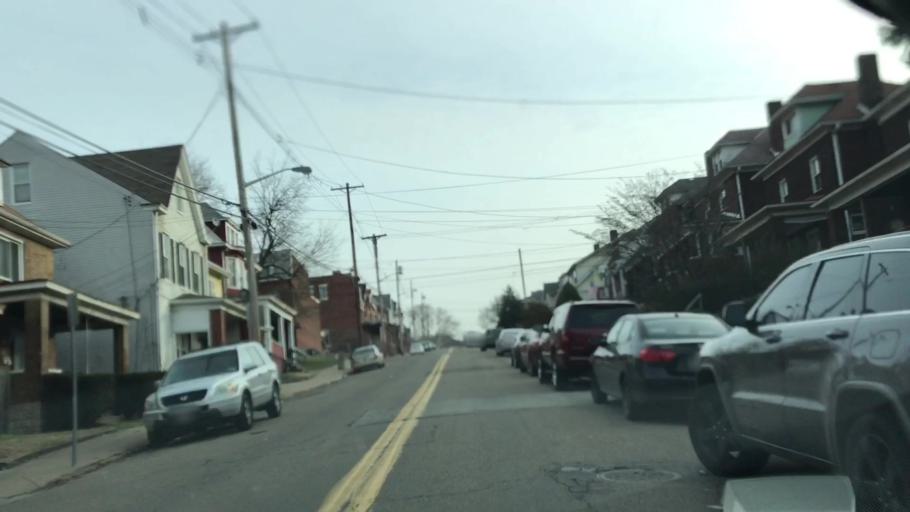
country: US
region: Pennsylvania
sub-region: Allegheny County
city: Bellevue
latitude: 40.4679
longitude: -80.0307
